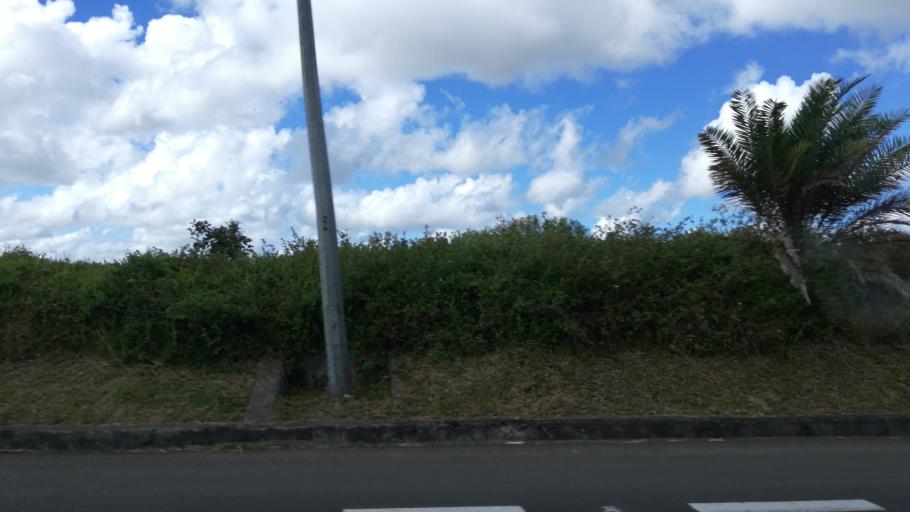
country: MU
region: Moka
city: Providence
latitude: -20.2440
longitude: 57.6141
